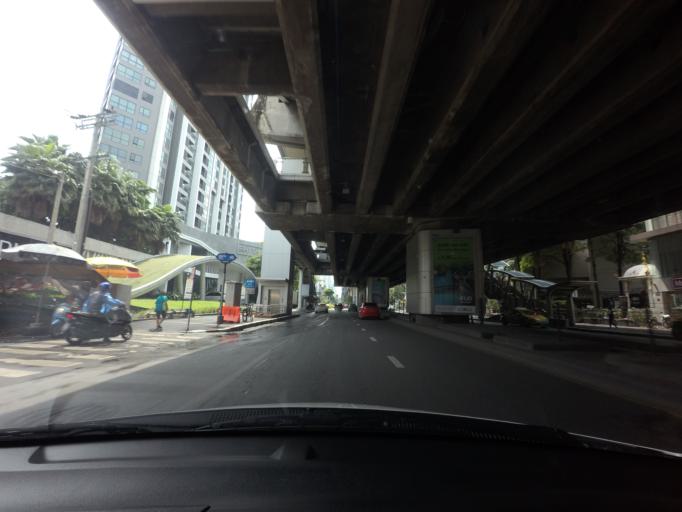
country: TH
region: Bangkok
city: Watthana
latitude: 13.7151
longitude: 100.5912
